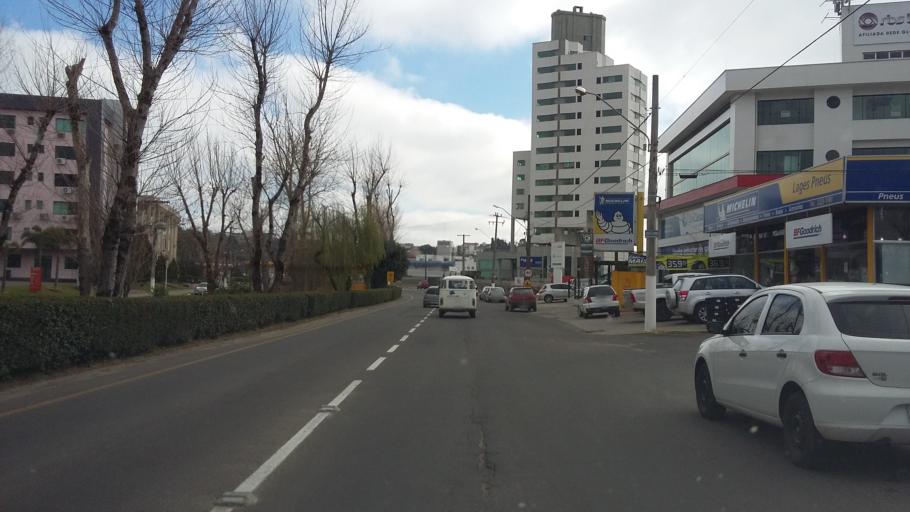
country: BR
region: Santa Catarina
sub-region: Lages
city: Lages
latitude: -27.8097
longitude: -50.3180
